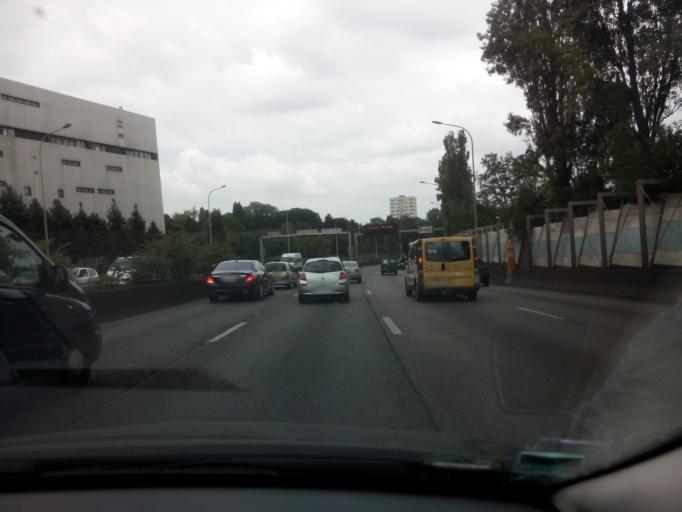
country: FR
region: Ile-de-France
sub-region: Departement de Seine-Saint-Denis
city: Le Pre-Saint-Gervais
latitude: 48.8811
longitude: 2.4038
